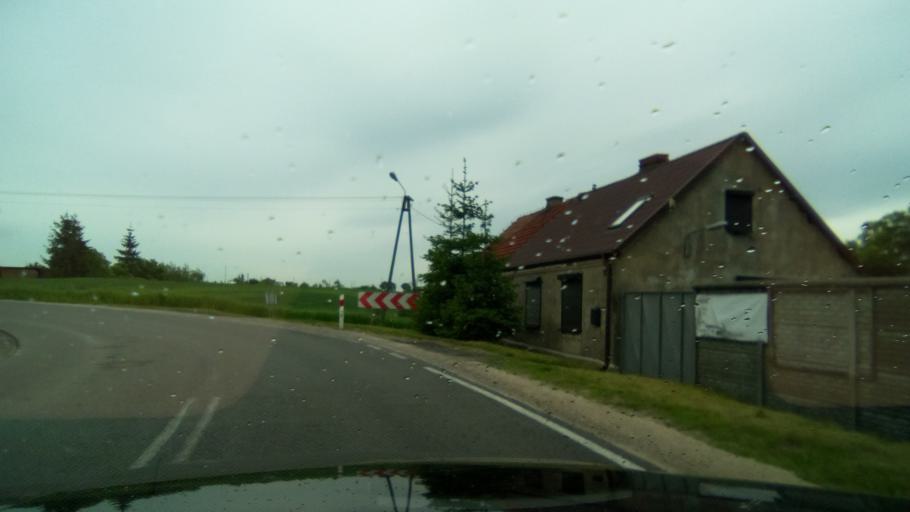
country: PL
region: Pomeranian Voivodeship
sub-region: Powiat chojnicki
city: Chojnice
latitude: 53.6704
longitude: 17.5318
